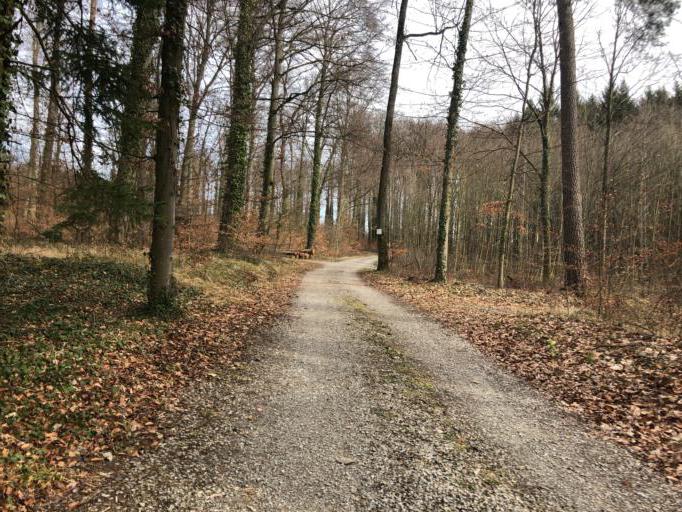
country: DE
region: Baden-Wuerttemberg
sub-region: Karlsruhe Region
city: Wiernsheim
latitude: 48.9228
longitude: 8.8791
